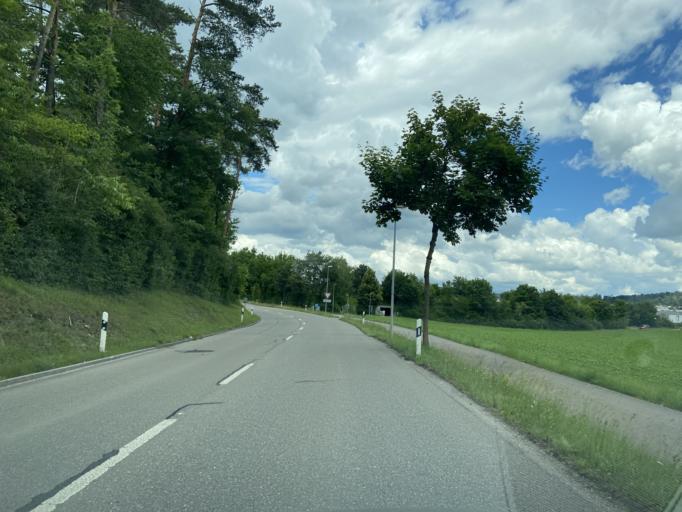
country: CH
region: Zurich
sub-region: Bezirk Buelach
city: Bassersdorf
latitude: 47.4340
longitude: 8.6269
